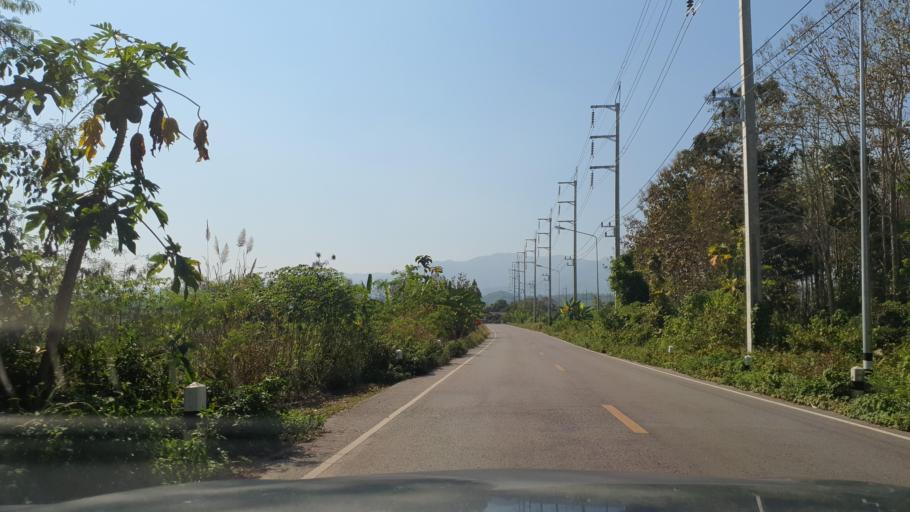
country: TH
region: Chiang Rai
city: Mae Lao
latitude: 19.8044
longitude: 99.6827
